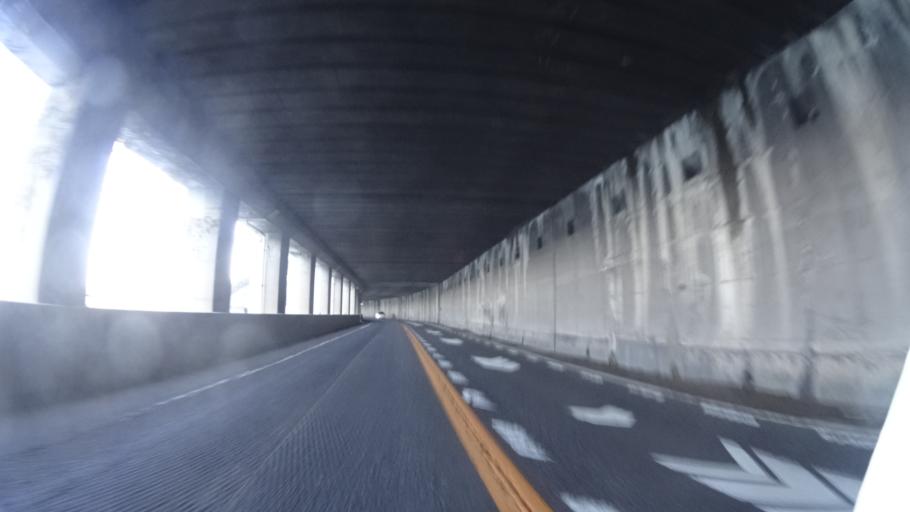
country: JP
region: Fukui
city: Tsuruga
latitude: 35.7305
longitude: 136.0968
